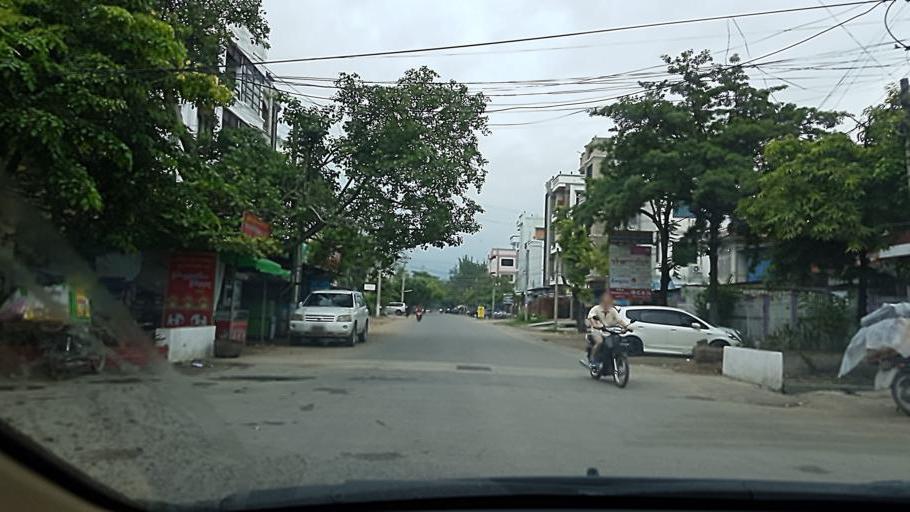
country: MM
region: Mandalay
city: Mandalay
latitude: 21.9794
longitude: 96.0969
